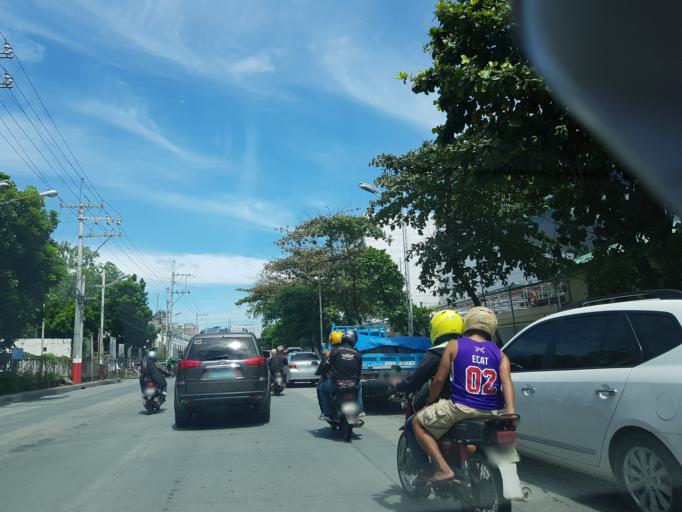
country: PH
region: Calabarzon
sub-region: Province of Rizal
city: Pateros
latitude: 14.5292
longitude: 121.0618
